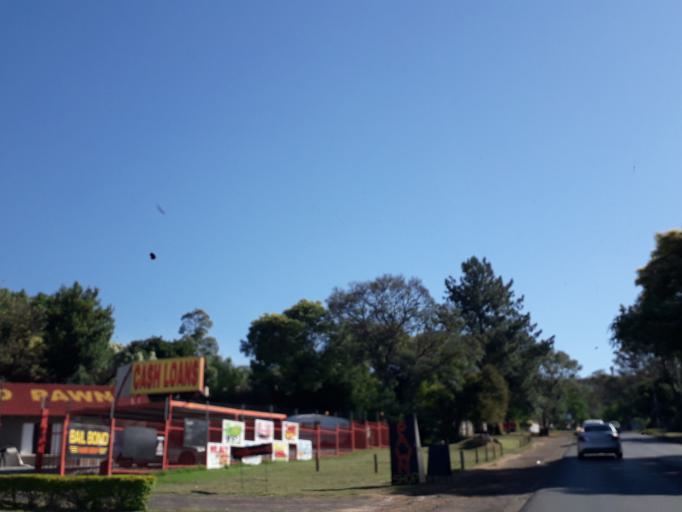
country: ZA
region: Gauteng
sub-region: City of Johannesburg Metropolitan Municipality
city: Roodepoort
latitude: -26.1466
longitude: 27.9521
